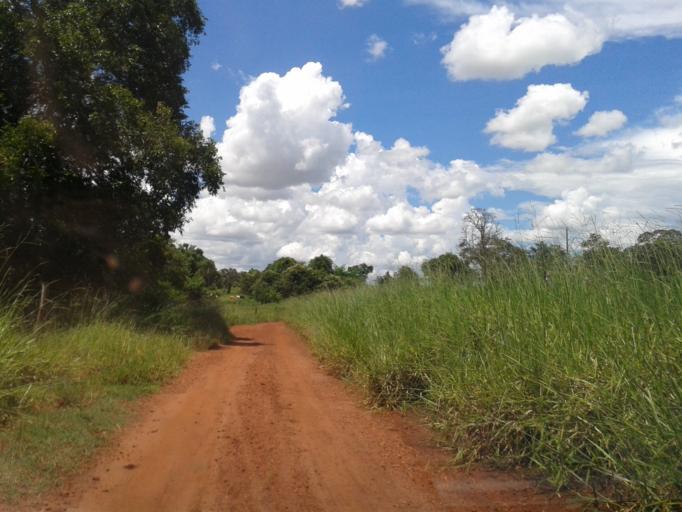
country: BR
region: Minas Gerais
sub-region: Capinopolis
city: Capinopolis
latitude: -18.7939
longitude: -49.8359
